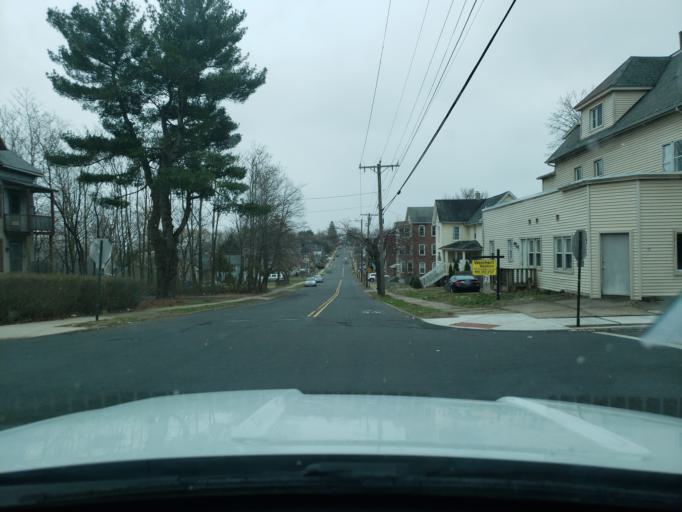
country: US
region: Connecticut
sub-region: Hartford County
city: New Britain
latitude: 41.6692
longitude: -72.7607
